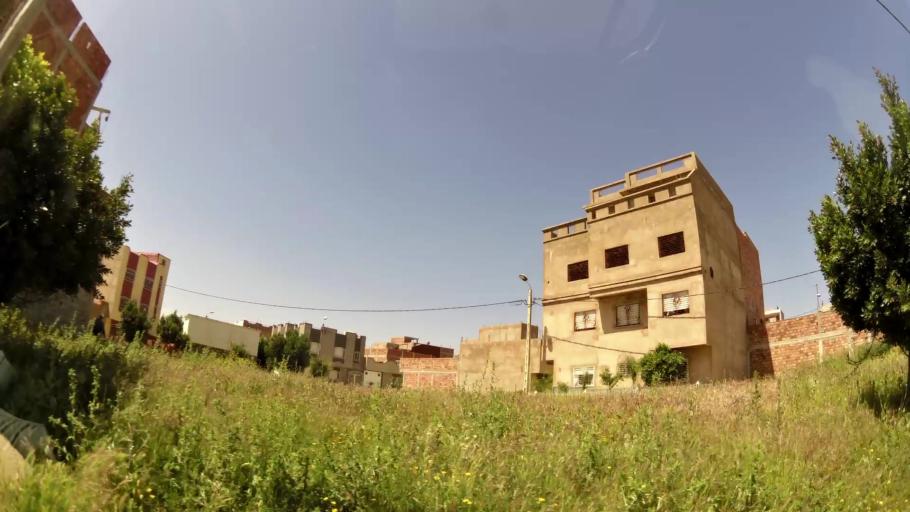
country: MA
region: Rabat-Sale-Zemmour-Zaer
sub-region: Khemisset
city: Khemisset
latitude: 33.8105
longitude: -6.0869
